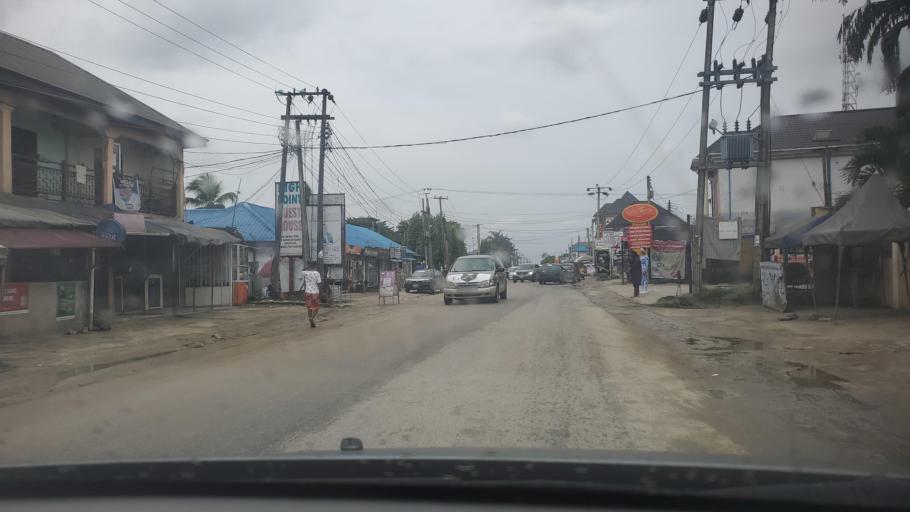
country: NG
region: Rivers
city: Port Harcourt
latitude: 4.8652
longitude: 6.9822
